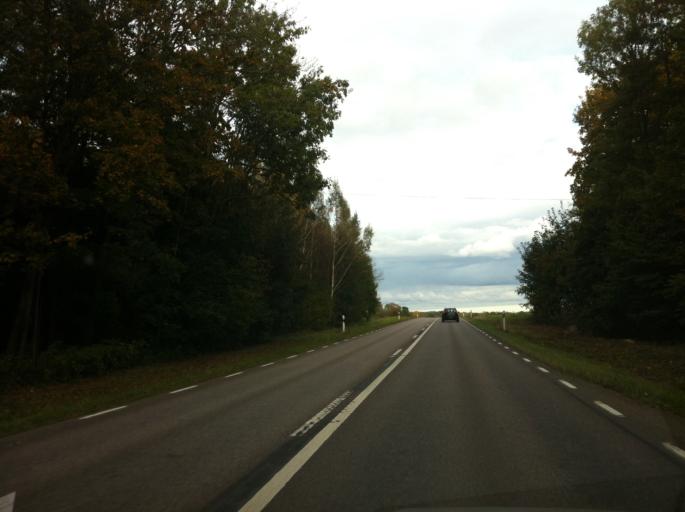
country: SE
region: OEstergoetland
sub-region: Motala Kommun
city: Motala
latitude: 58.4839
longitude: 14.9841
